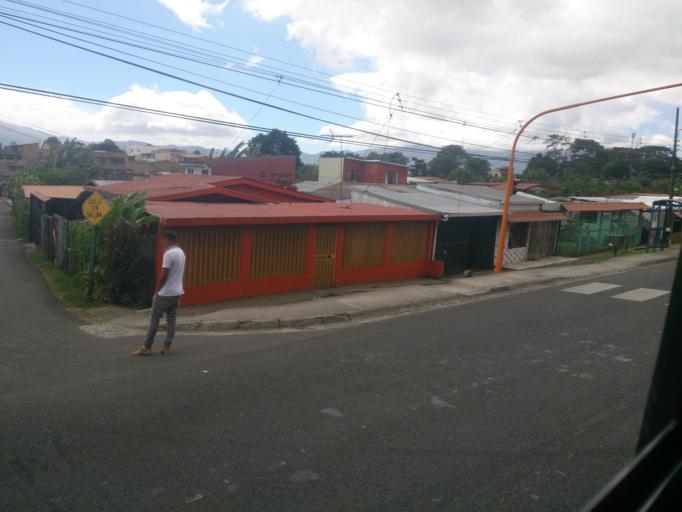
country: CR
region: San Jose
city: Granadilla
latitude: 9.9269
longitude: -84.0211
